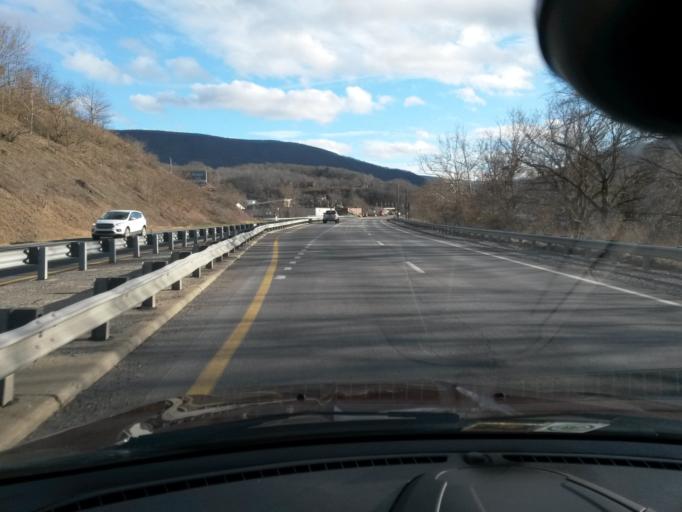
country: US
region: Virginia
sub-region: Giles County
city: Narrows
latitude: 37.3844
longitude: -80.8257
